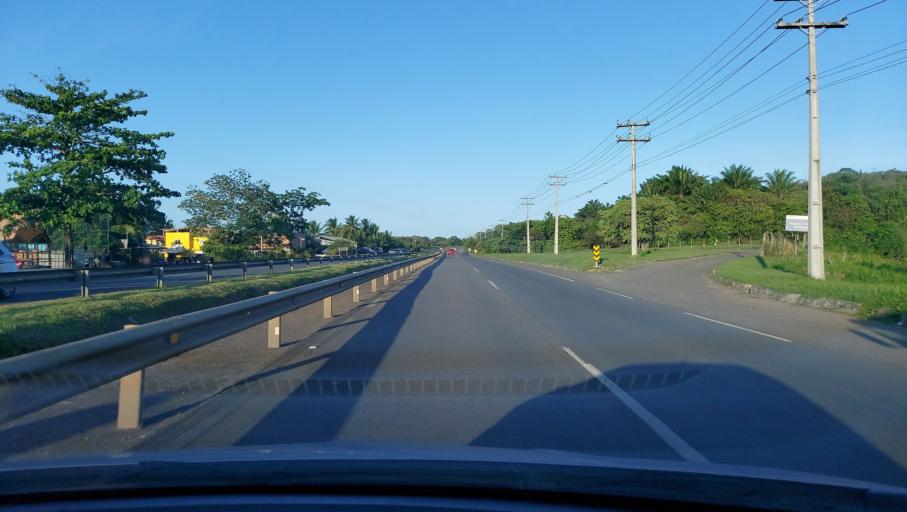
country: BR
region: Bahia
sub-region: Lauro De Freitas
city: Lauro de Freitas
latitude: -12.8043
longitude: -38.2267
